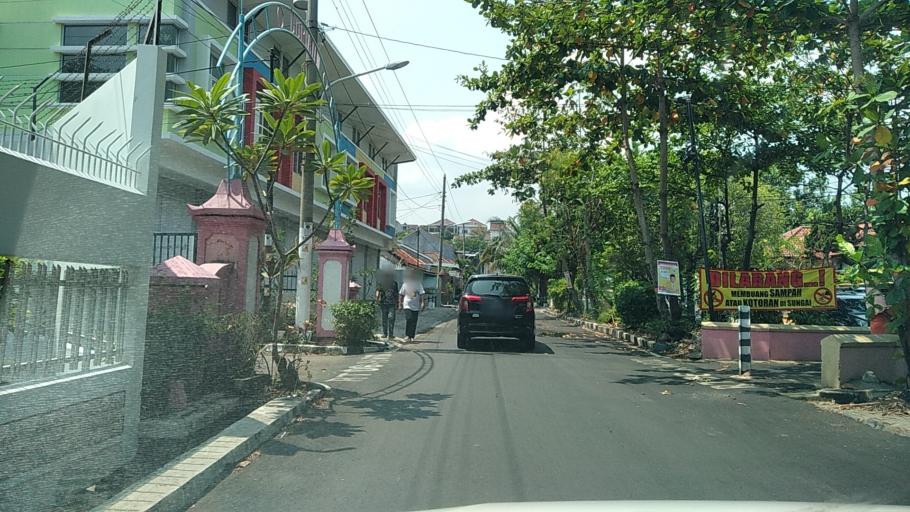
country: ID
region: Central Java
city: Semarang
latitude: -7.0084
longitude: 110.4391
